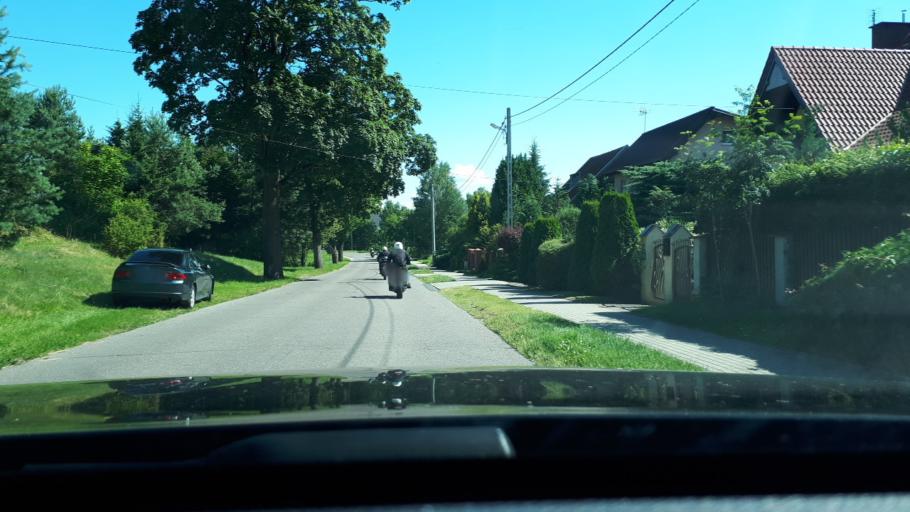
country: PL
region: Warmian-Masurian Voivodeship
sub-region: Powiat olsztynski
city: Stawiguda
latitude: 53.6545
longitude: 20.4029
